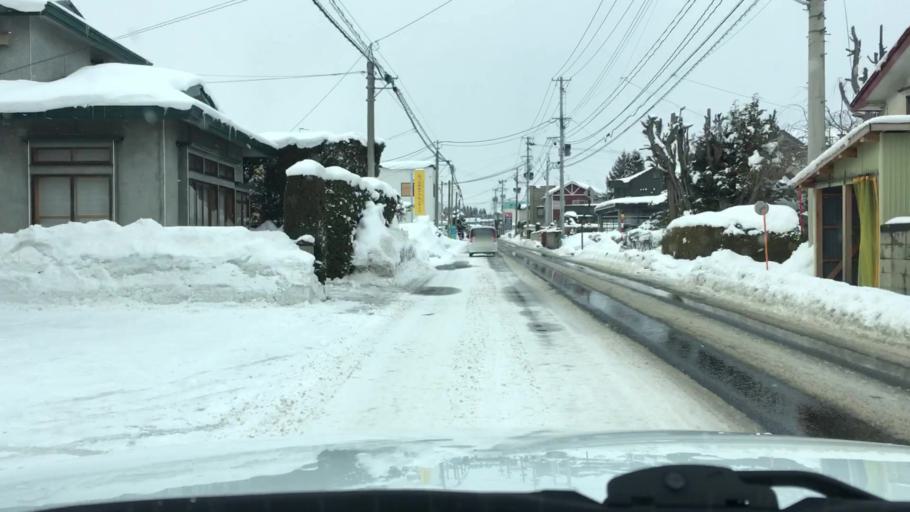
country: JP
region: Aomori
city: Hirosaki
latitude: 40.5790
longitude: 140.5022
